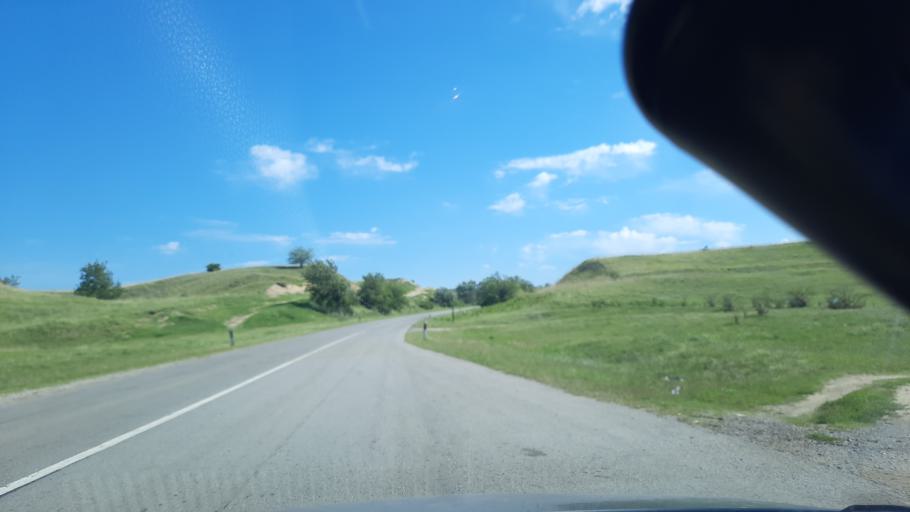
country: RO
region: Caras-Severin
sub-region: Comuna Socol
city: Socol
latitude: 44.8624
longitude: 21.3075
